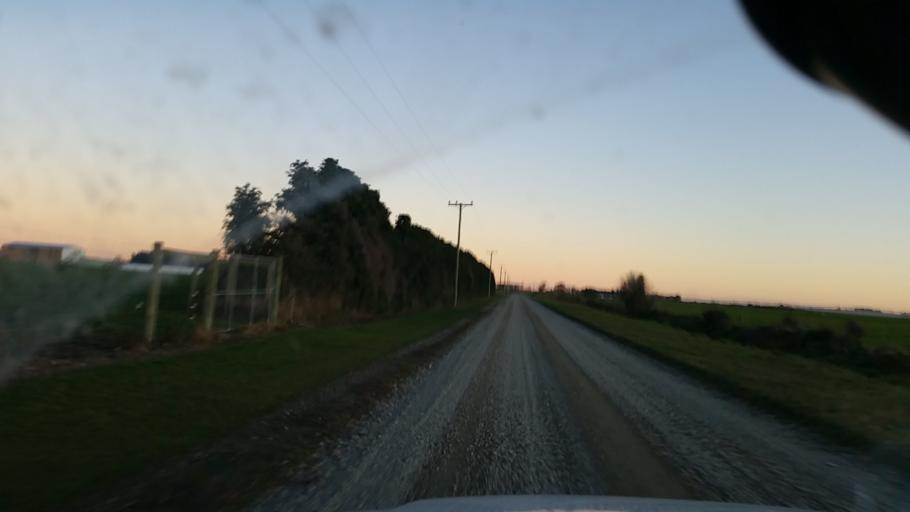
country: NZ
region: Canterbury
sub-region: Ashburton District
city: Tinwald
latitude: -44.0489
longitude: 171.6631
